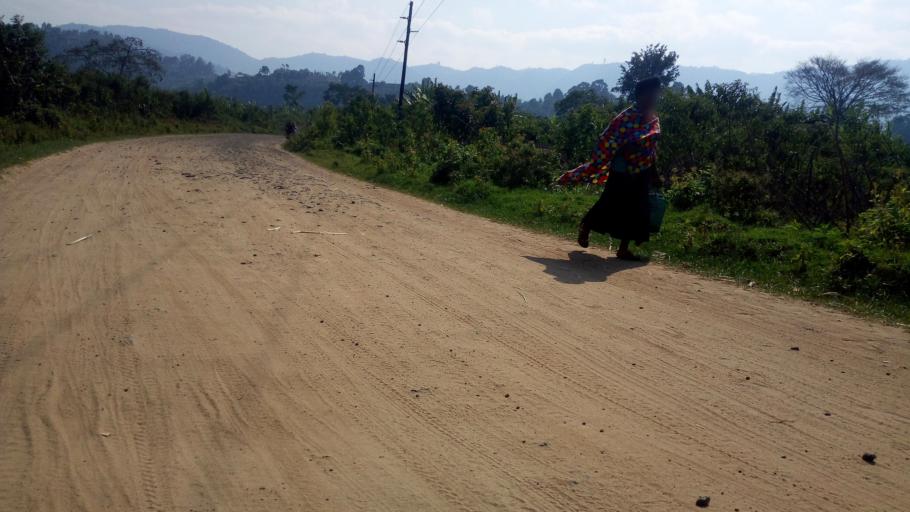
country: UG
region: Western Region
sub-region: Kisoro District
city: Kisoro
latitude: -1.2264
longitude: 29.7129
